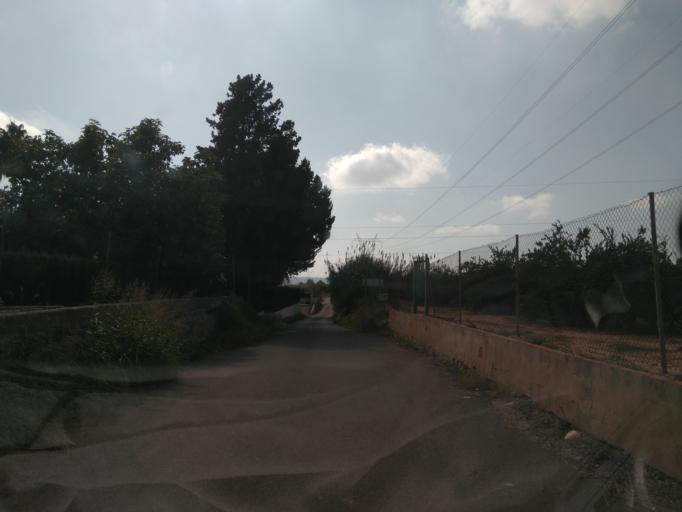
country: ES
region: Valencia
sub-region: Provincia de Valencia
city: Masalaves
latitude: 39.1732
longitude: -0.5527
